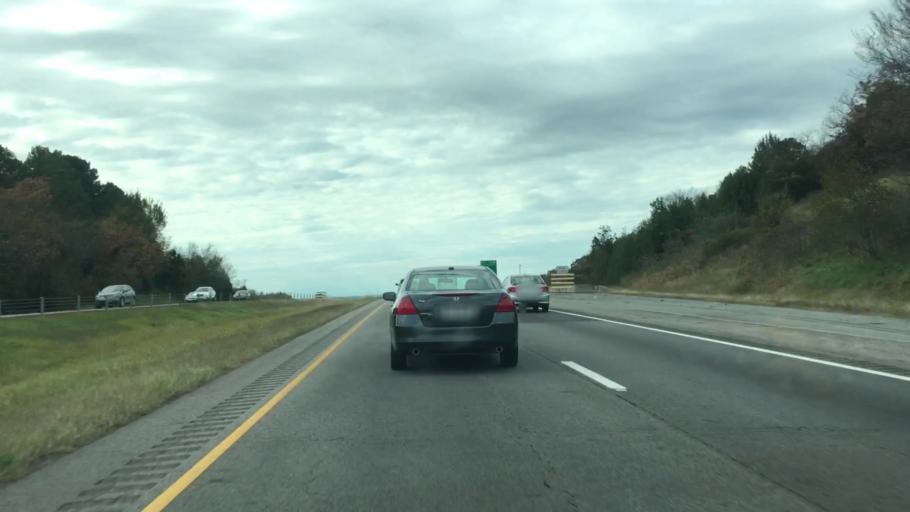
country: US
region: Arkansas
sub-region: Conway County
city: Morrilton
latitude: 35.1704
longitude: -92.6943
